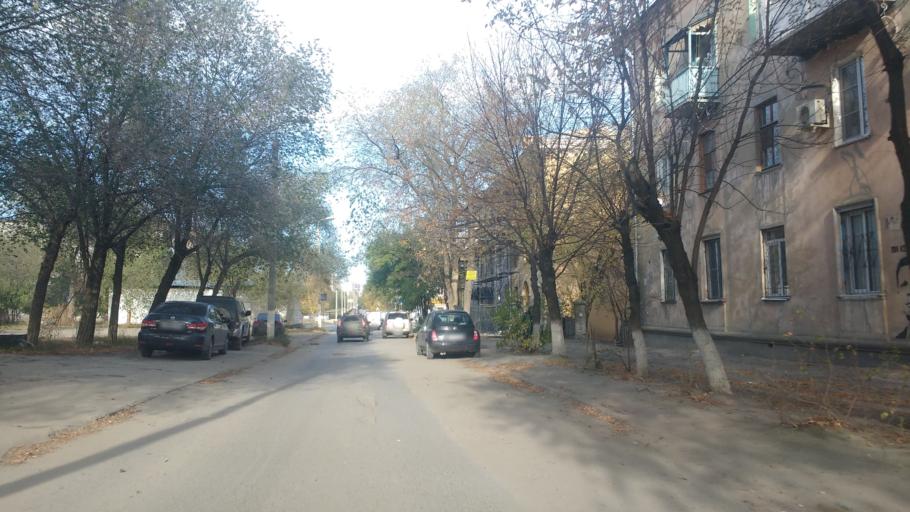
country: RU
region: Volgograd
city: Krasnoslobodsk
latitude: 48.7667
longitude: 44.5544
